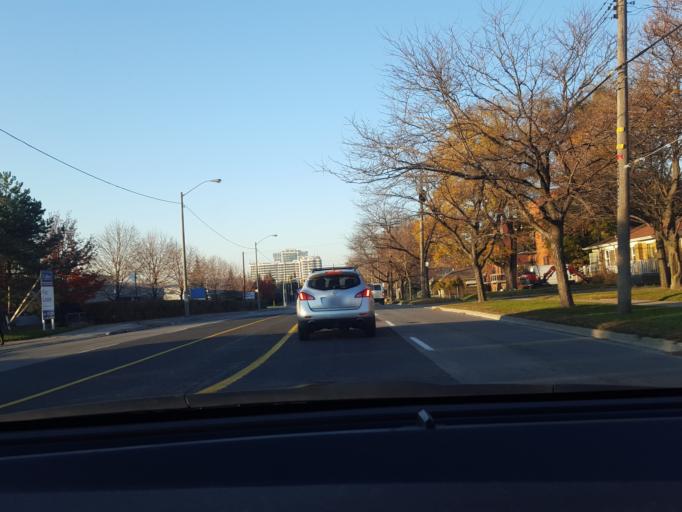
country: CA
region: Ontario
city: Scarborough
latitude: 43.7408
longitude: -79.2821
